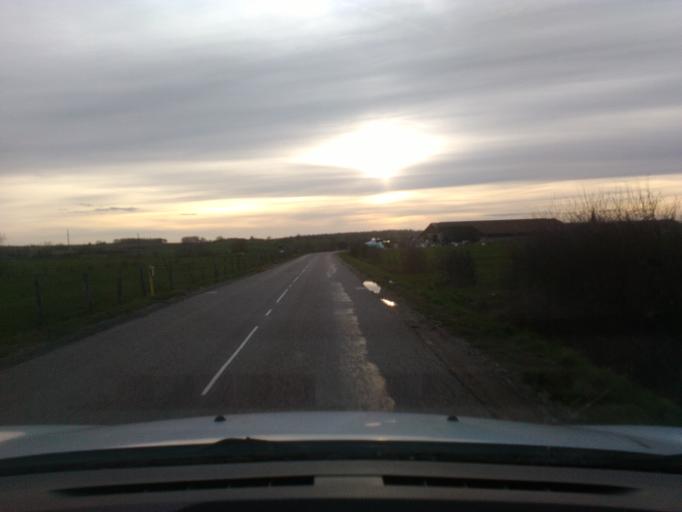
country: FR
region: Lorraine
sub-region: Departement des Vosges
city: Chatel-sur-Moselle
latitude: 48.3485
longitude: 6.4434
